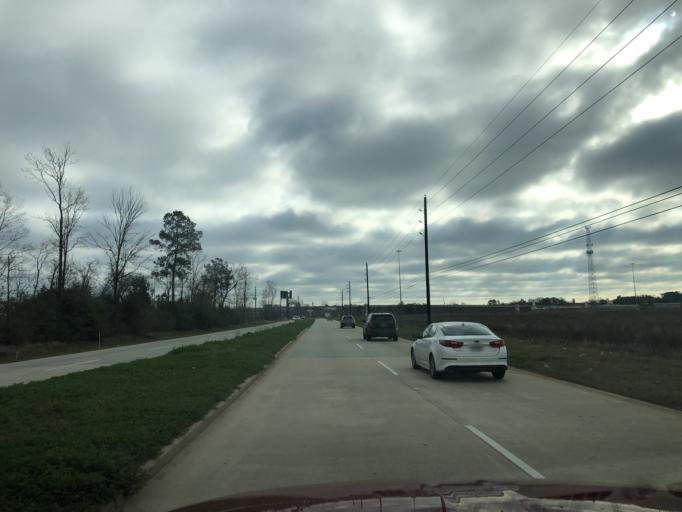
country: US
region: Texas
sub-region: Harris County
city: Spring
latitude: 30.0829
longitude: -95.4424
